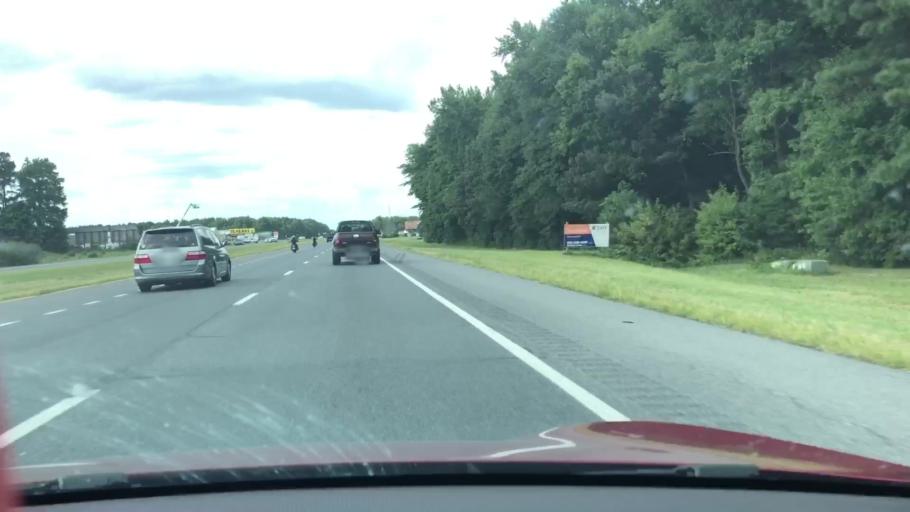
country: US
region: Delaware
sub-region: Sussex County
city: Delmar
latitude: 38.4804
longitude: -75.5576
